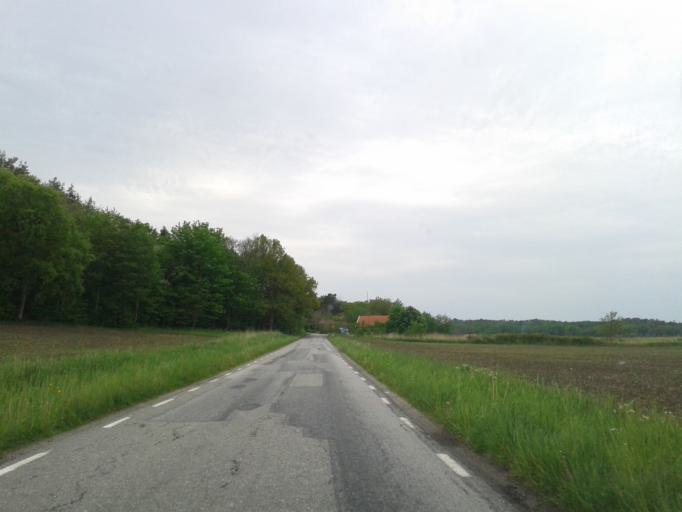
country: SE
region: Vaestra Goetaland
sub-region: Kungalvs Kommun
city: Kode
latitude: 57.8730
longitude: 11.7278
